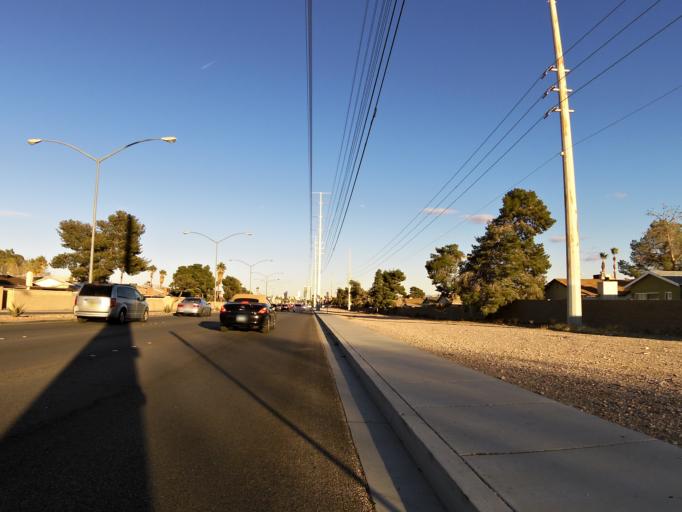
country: US
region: Nevada
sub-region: Clark County
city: Spring Valley
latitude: 36.1144
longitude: -115.2464
